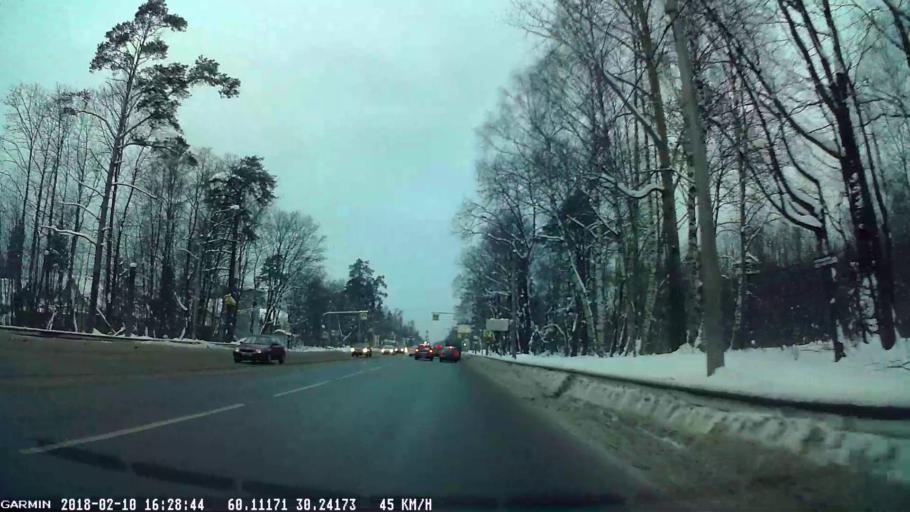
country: RU
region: St.-Petersburg
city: Levashovo
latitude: 60.1119
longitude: 30.2416
